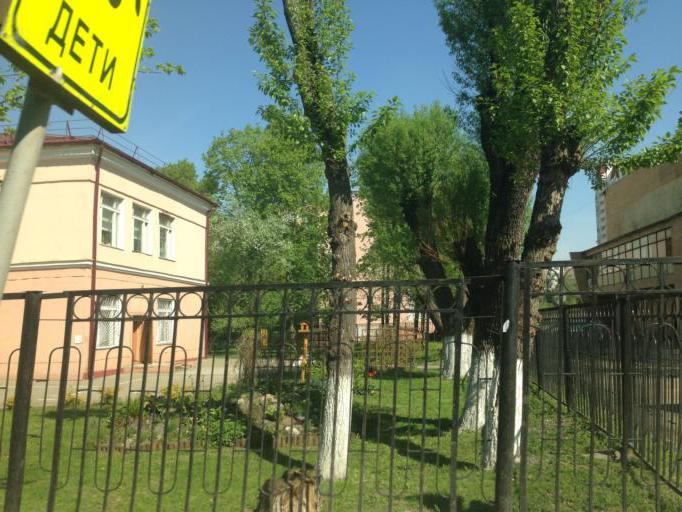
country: RU
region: Moskovskaya
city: Balashikha
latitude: 55.8142
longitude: 37.9648
